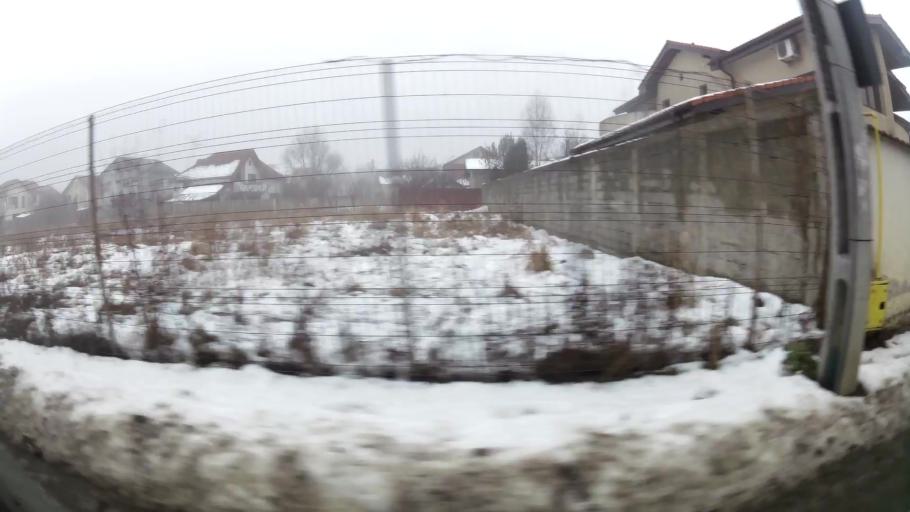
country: RO
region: Ilfov
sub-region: Comuna Chiajna
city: Chiajna
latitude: 44.4515
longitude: 25.9904
